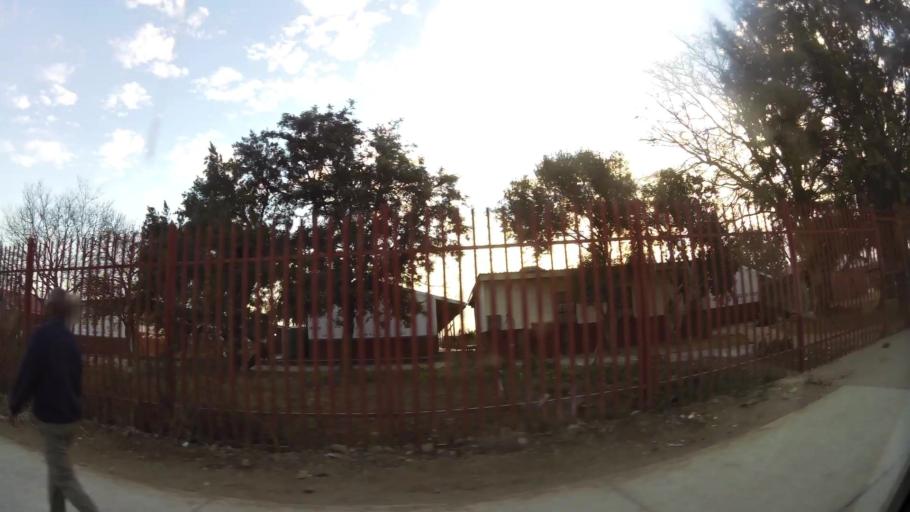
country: ZA
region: Gauteng
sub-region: City of Tshwane Metropolitan Municipality
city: Pretoria
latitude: -25.7159
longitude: 28.3490
